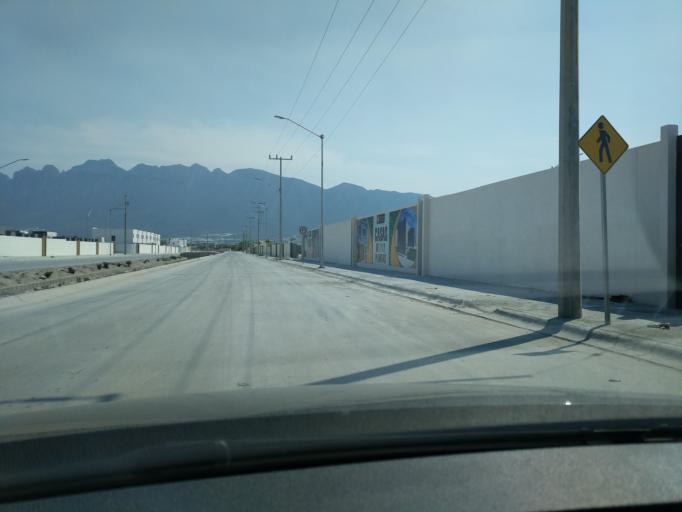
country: MX
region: Nuevo Leon
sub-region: Garcia
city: Valle de Lincoln
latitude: 25.7968
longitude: -100.4716
